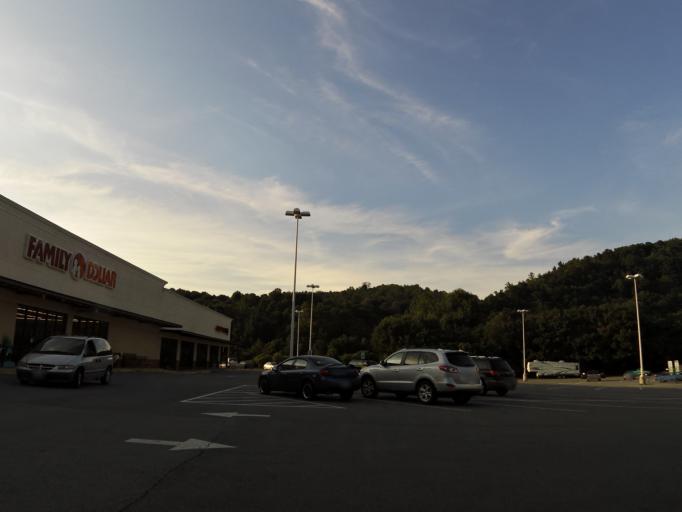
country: US
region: Virginia
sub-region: Washington County
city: Emory
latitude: 36.6408
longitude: -81.7996
